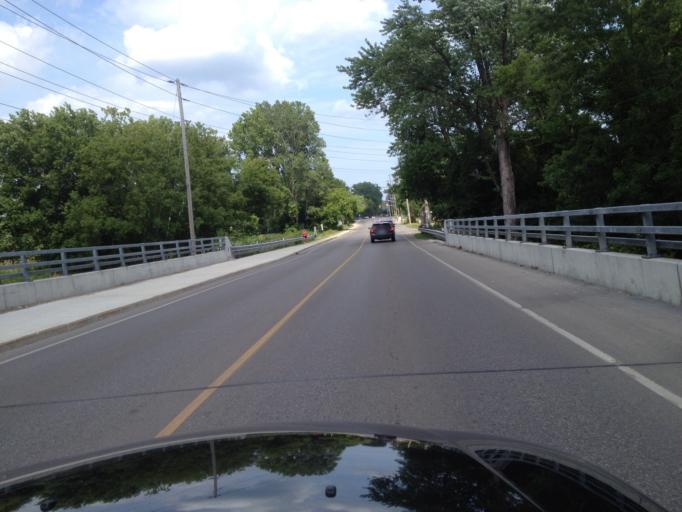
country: CA
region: Ontario
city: London
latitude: 43.0222
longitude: -81.2524
